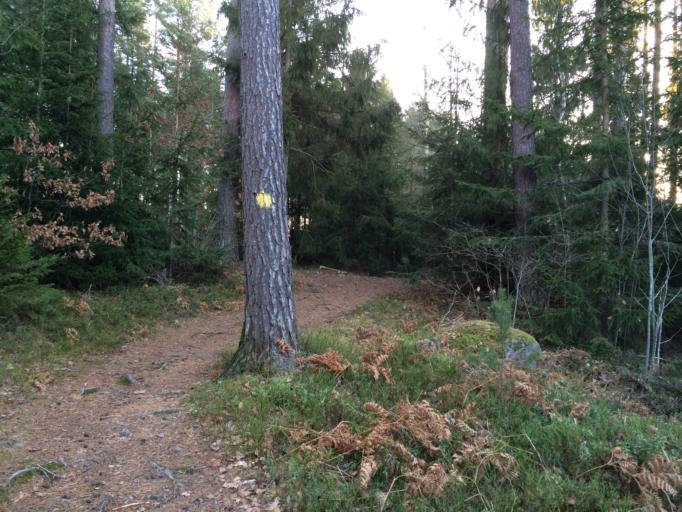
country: SE
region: Vaestmanland
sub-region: Hallstahammars Kommun
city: Hallstahammar
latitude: 59.6175
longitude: 16.1996
